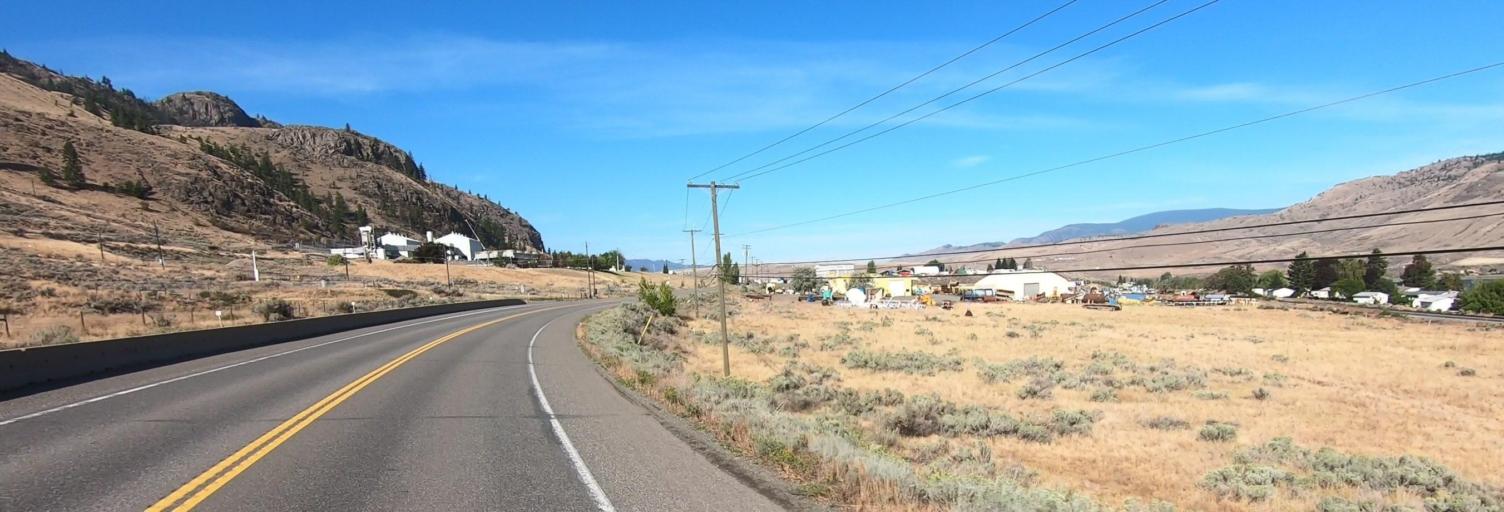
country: CA
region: British Columbia
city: Logan Lake
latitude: 50.7501
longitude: -120.8487
